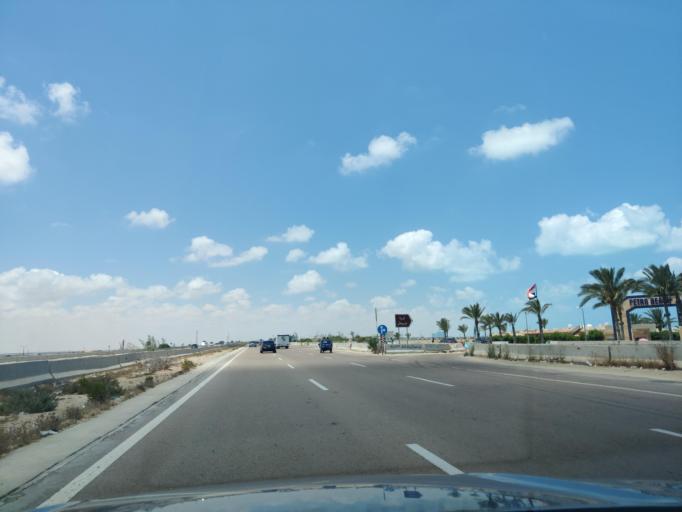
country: EG
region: Muhafazat Matruh
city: Al `Alamayn
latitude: 30.8125
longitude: 29.0859
